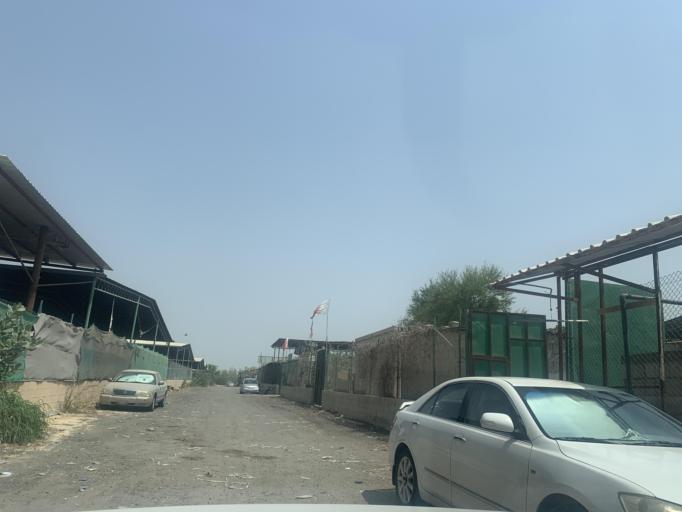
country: BH
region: Central Governorate
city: Madinat Hamad
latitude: 26.1412
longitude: 50.4786
